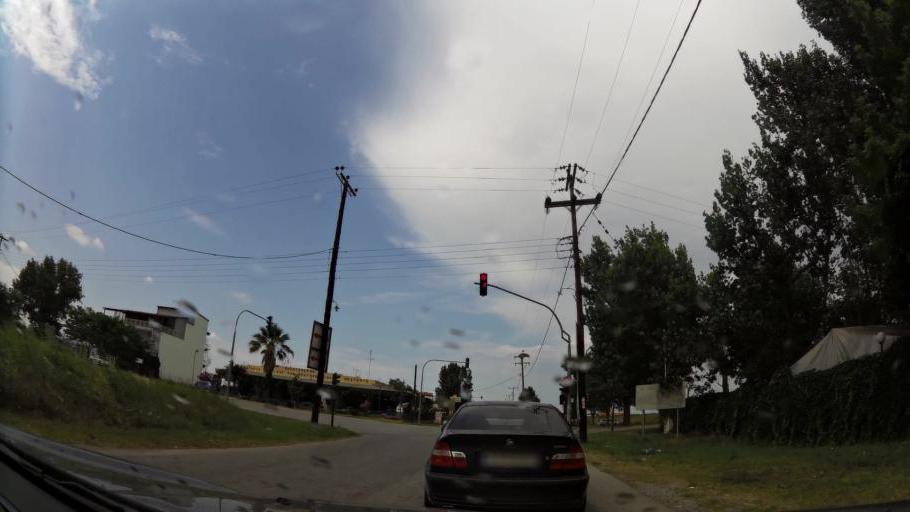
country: GR
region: Central Macedonia
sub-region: Nomos Pierias
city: Korinos
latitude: 40.3065
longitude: 22.6153
